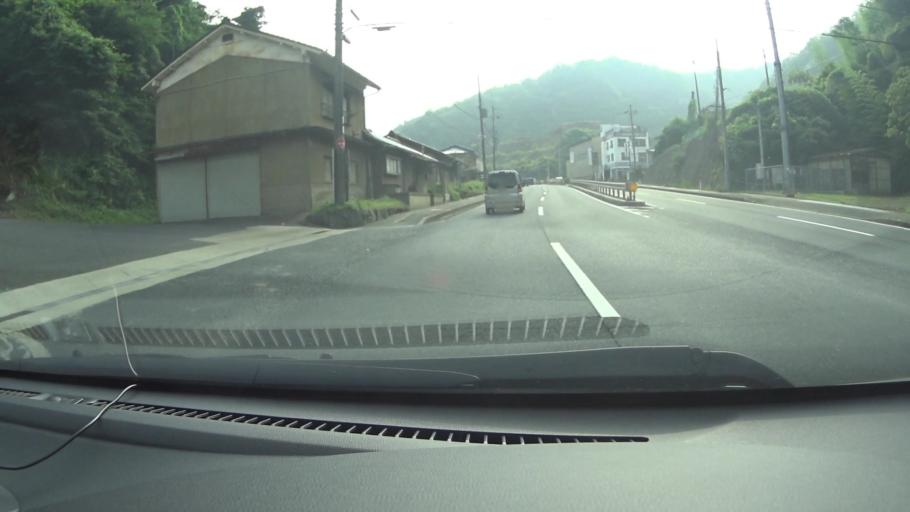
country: JP
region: Kyoto
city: Kameoka
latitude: 34.9905
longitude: 135.6079
